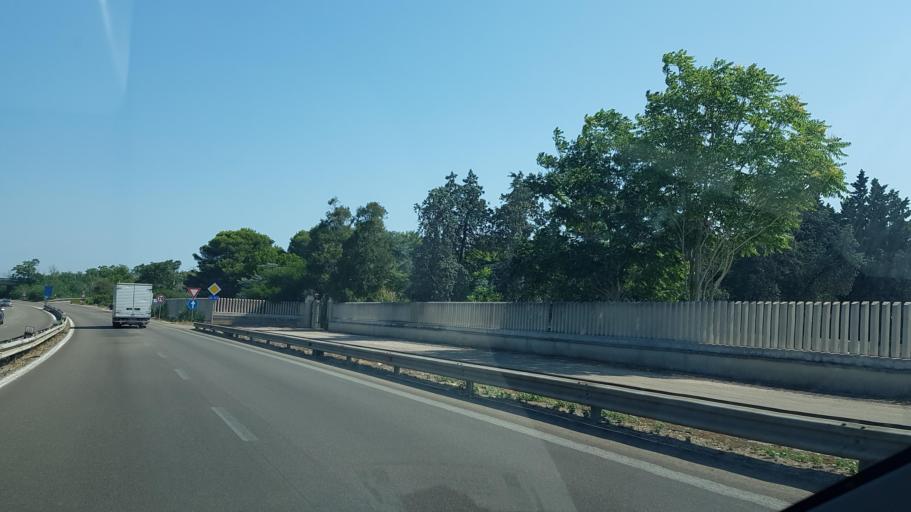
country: IT
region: Apulia
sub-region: Provincia di Lecce
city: Muro Leccese
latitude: 40.1139
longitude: 18.3208
